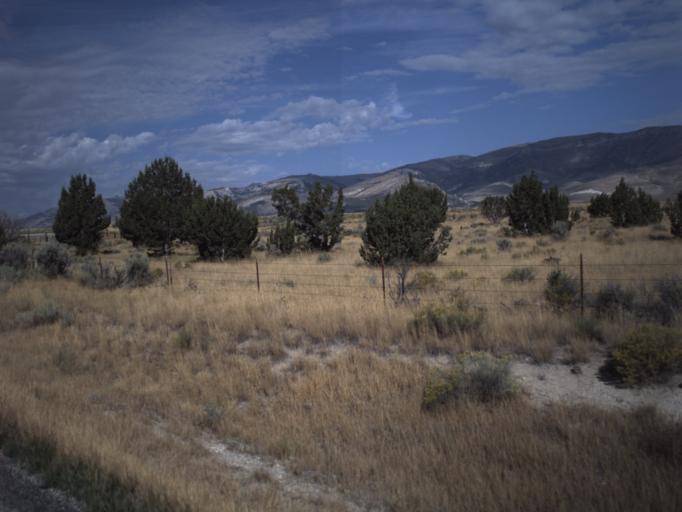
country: US
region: Idaho
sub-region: Cassia County
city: Burley
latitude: 41.8173
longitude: -113.2698
